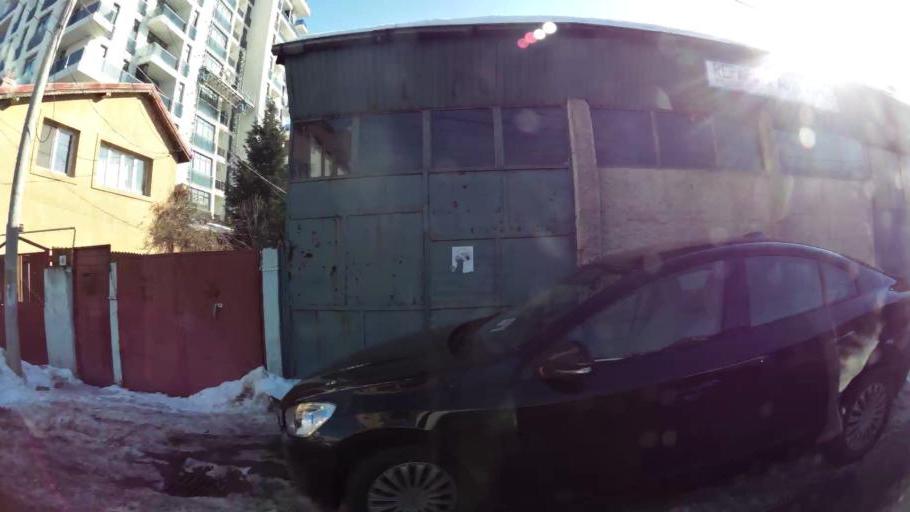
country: RO
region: Bucuresti
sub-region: Municipiul Bucuresti
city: Bucharest
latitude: 44.4699
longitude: 26.1110
